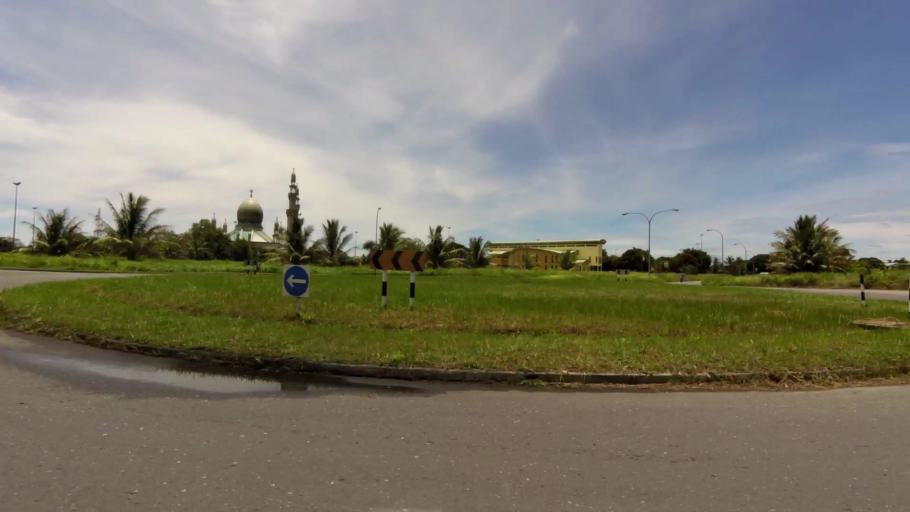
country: BN
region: Belait
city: Kuala Belait
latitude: 4.5834
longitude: 114.2319
